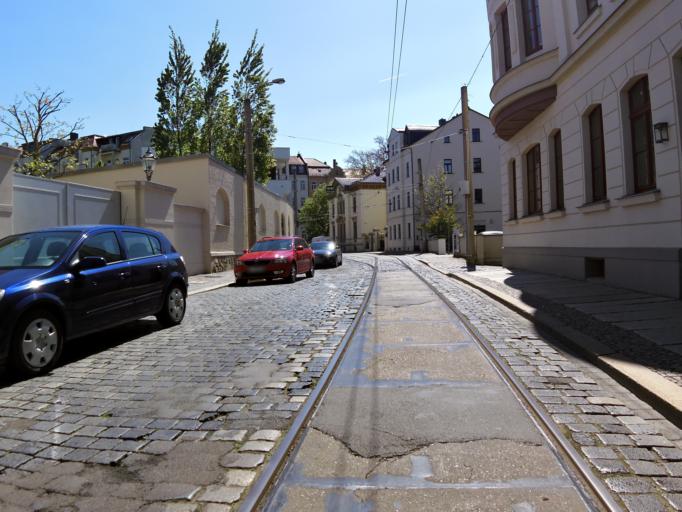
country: DE
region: Saxony
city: Leipzig
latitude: 51.3578
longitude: 12.3629
